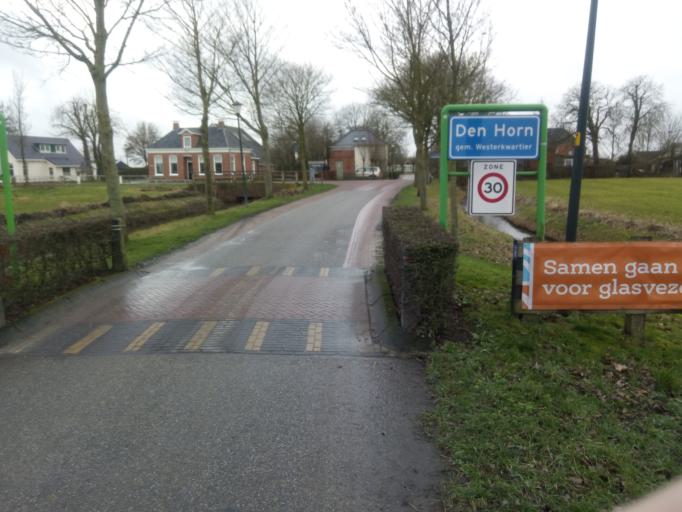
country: NL
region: Groningen
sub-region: Gemeente Zuidhorn
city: Aduard
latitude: 53.2285
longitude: 6.4501
